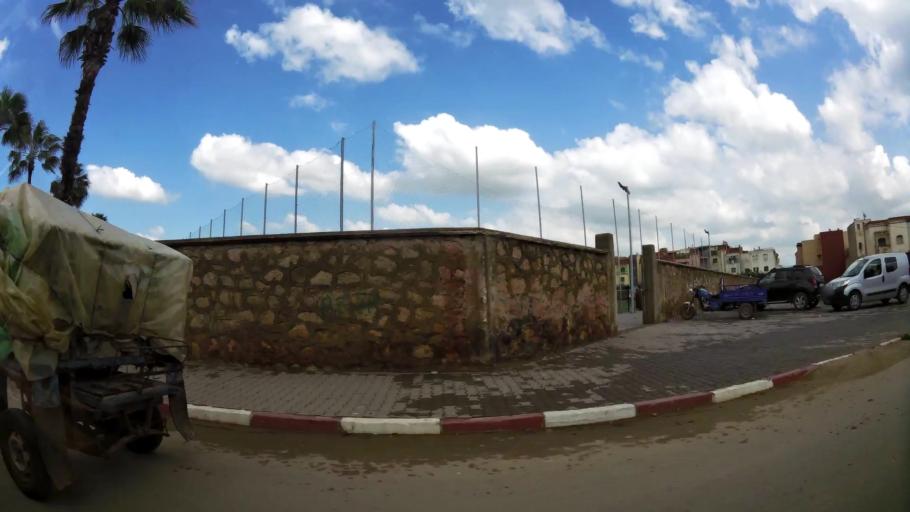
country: MA
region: Grand Casablanca
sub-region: Mediouna
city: Mediouna
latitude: 33.3728
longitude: -7.5309
